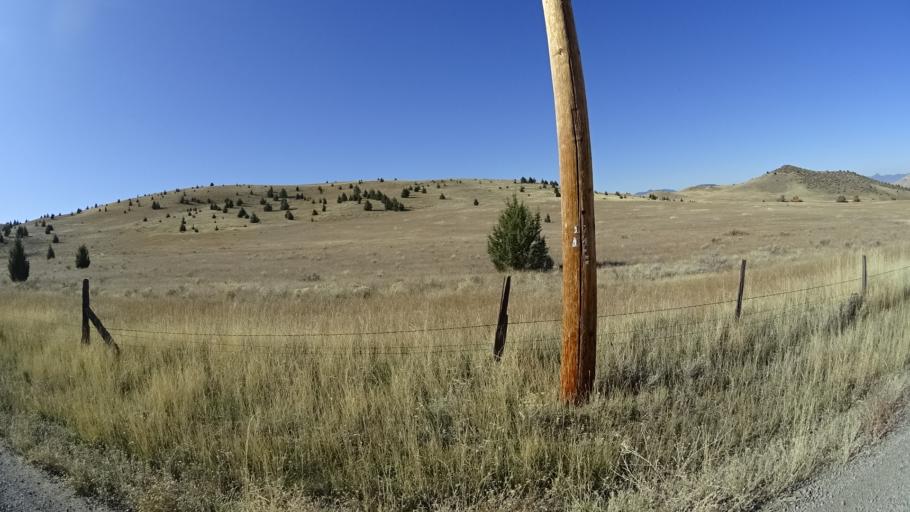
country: US
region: California
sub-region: Siskiyou County
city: Montague
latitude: 41.7796
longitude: -122.3589
